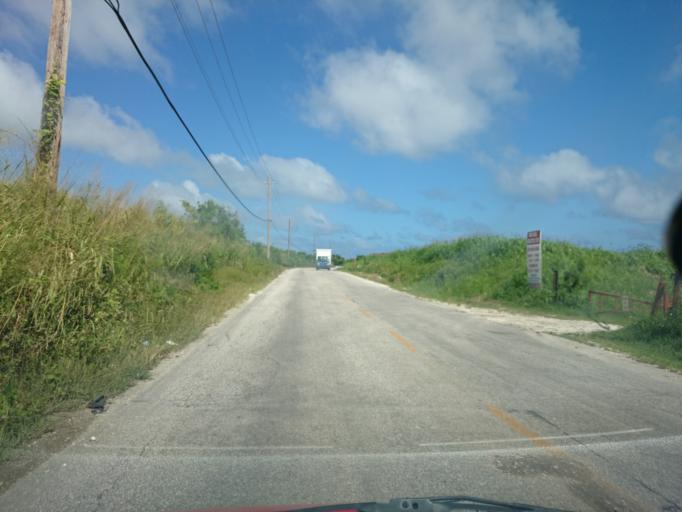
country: BB
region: Saint Philip
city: Crane
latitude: 13.0900
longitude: -59.4725
